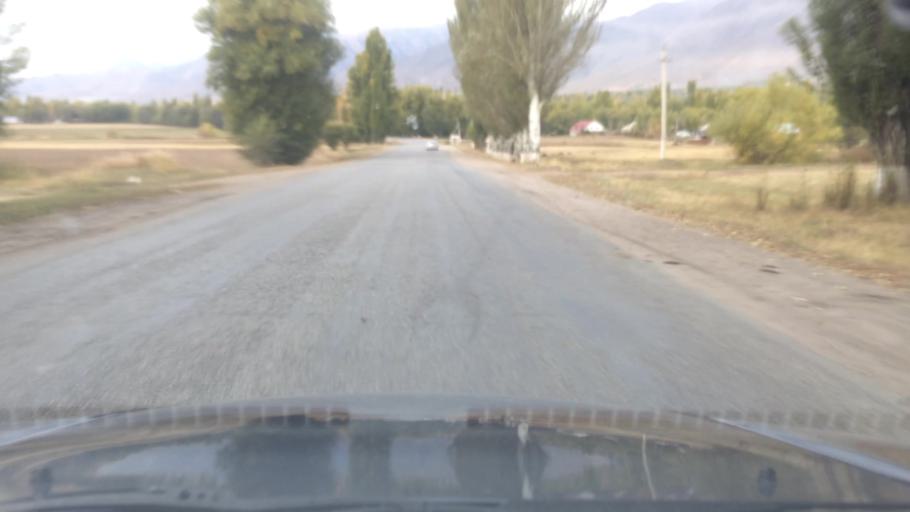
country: KG
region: Ysyk-Koel
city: Tyup
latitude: 42.7863
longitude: 78.2664
